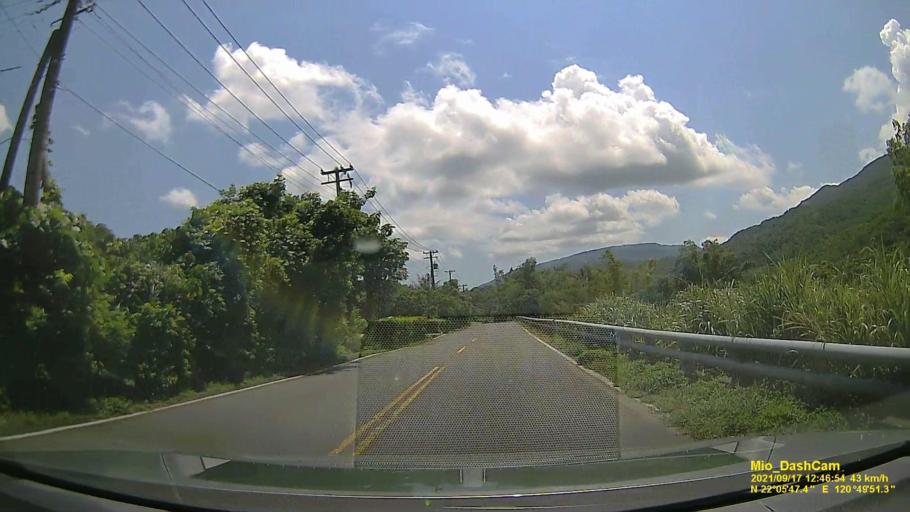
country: TW
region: Taiwan
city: Hengchun
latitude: 22.0964
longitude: 120.8309
